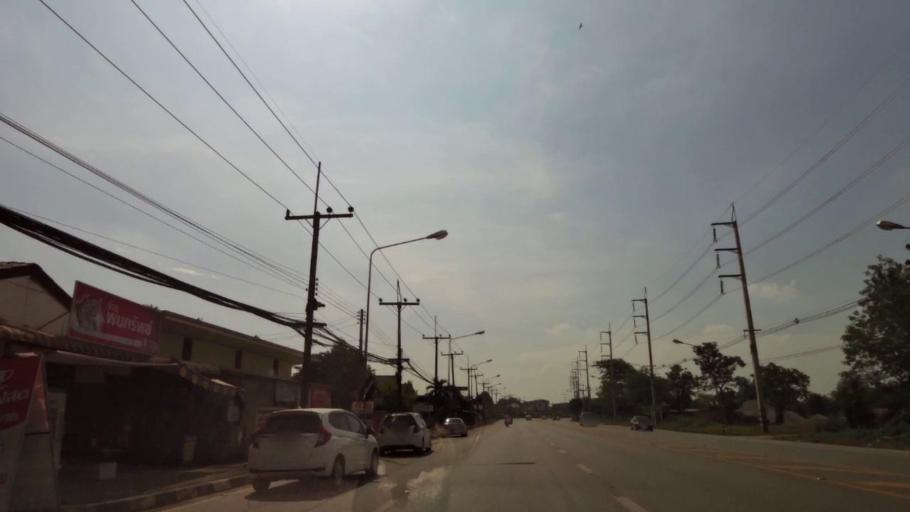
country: TH
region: Chiang Rai
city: Chiang Rai
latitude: 19.8864
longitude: 99.8007
